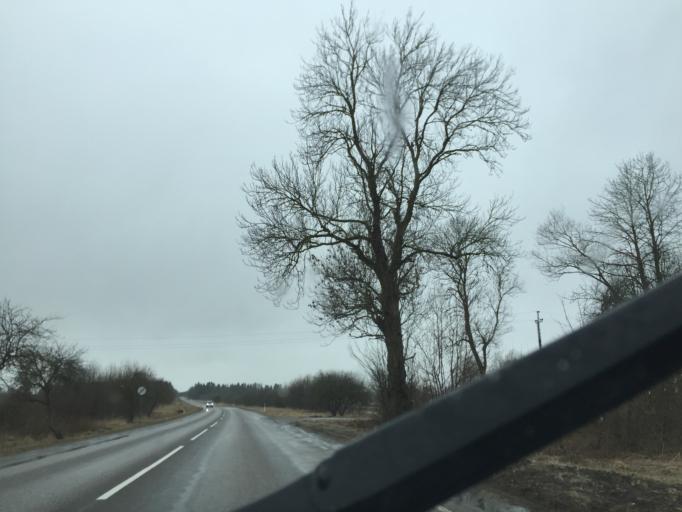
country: EE
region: Laeaene
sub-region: Ridala Parish
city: Uuemoisa
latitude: 58.8681
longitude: 23.6210
